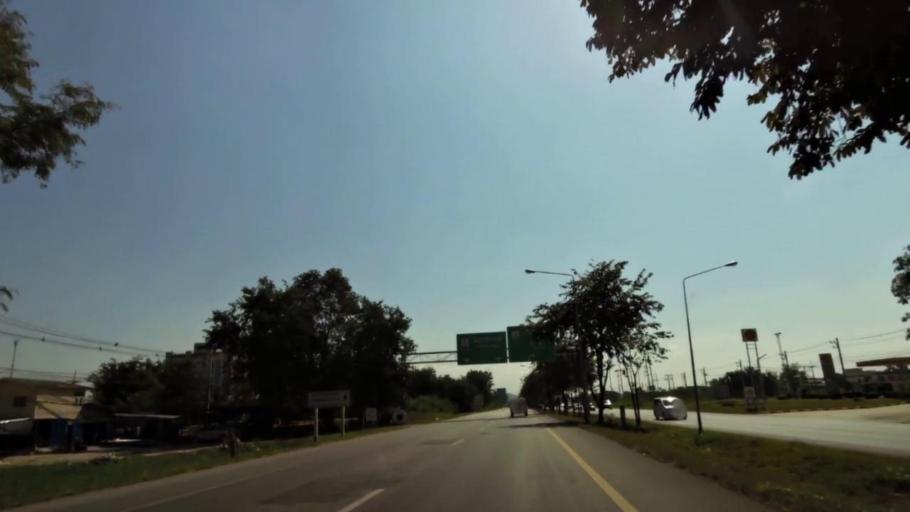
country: TH
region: Nakhon Sawan
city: Nakhon Sawan
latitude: 15.7731
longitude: 100.1213
